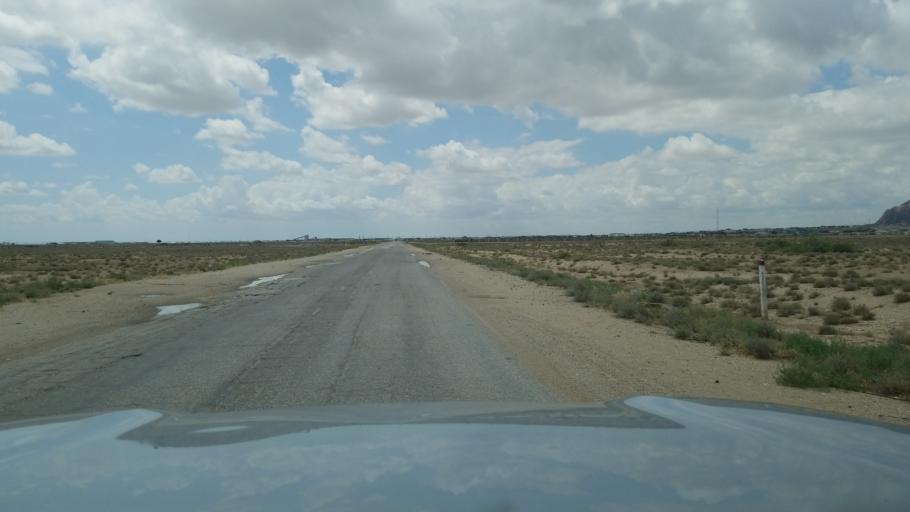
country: TM
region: Balkan
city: Balkanabat
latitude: 39.4869
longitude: 54.4157
